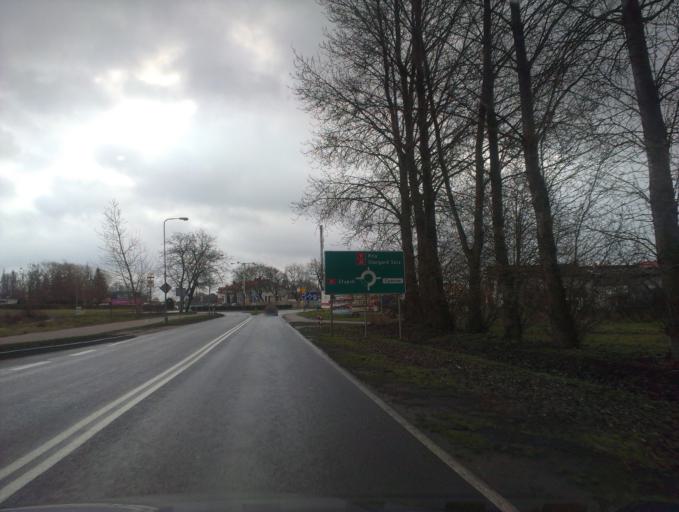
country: PL
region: West Pomeranian Voivodeship
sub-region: Powiat szczecinecki
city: Szczecinek
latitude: 53.7122
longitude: 16.7037
